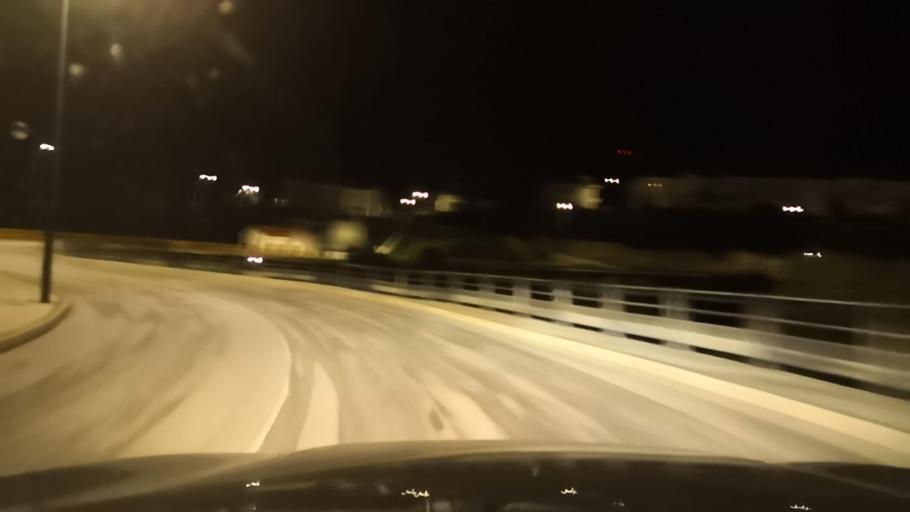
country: PT
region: Braganca
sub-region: Miranda do Douro
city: Miranda do Douro
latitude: 41.4990
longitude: -6.2752
